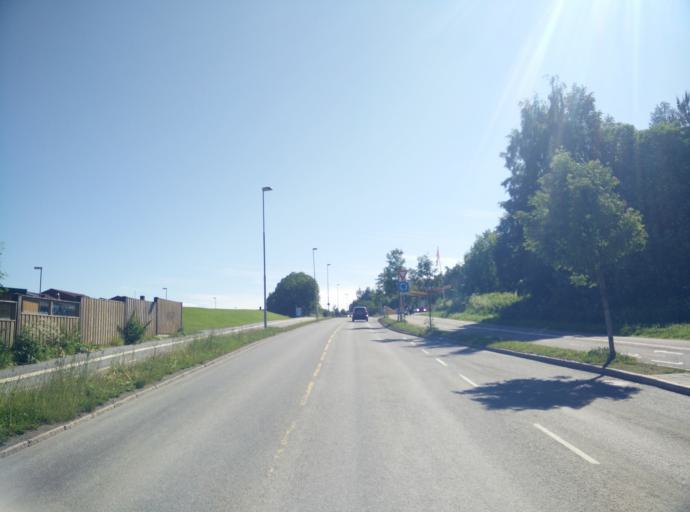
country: NO
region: Sor-Trondelag
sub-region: Trondheim
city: Trondheim
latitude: 63.4032
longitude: 10.3580
